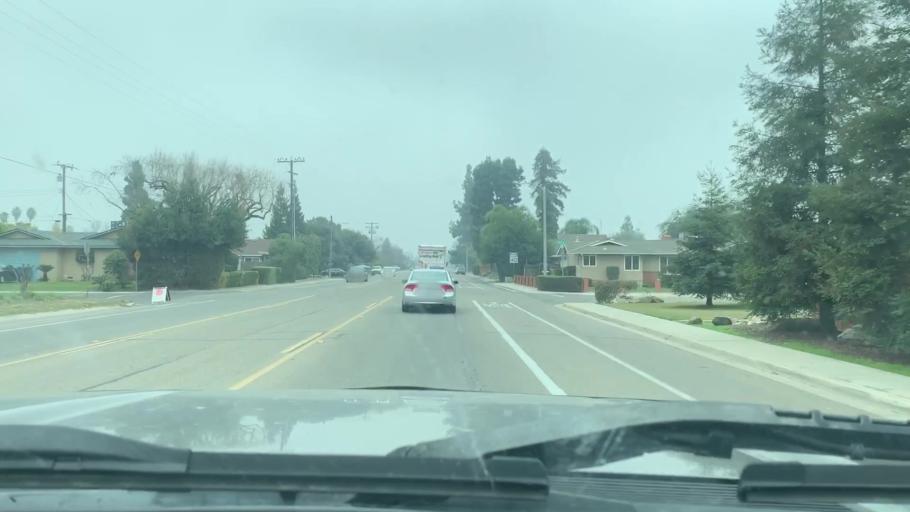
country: US
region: California
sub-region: Tulare County
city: Visalia
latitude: 36.3096
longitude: -119.3228
